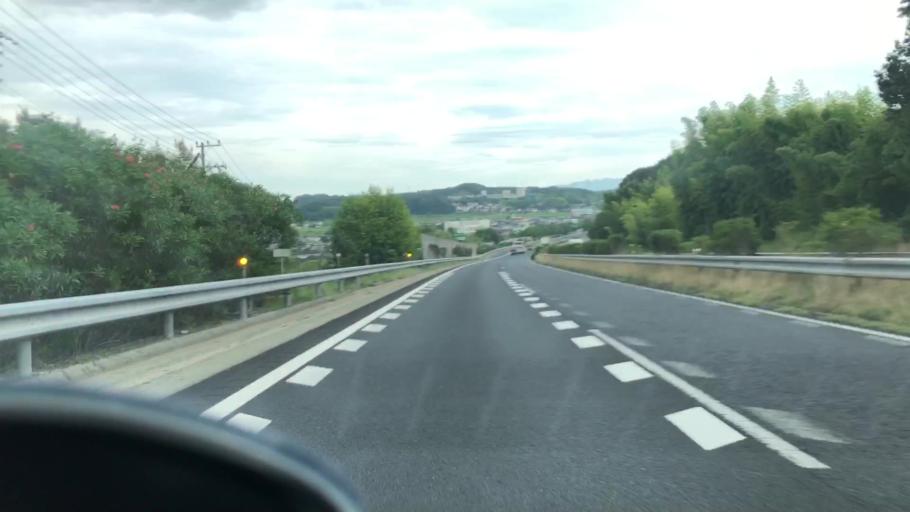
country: JP
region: Hyogo
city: Yashiro
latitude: 34.9095
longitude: 135.0589
